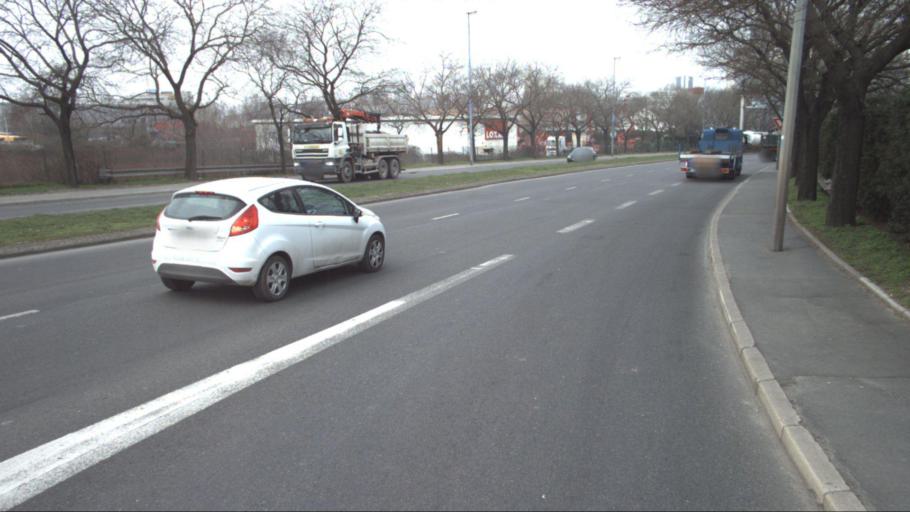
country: FR
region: Ile-de-France
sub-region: Departement des Hauts-de-Seine
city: Bois-Colombes
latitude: 48.9361
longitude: 2.2796
